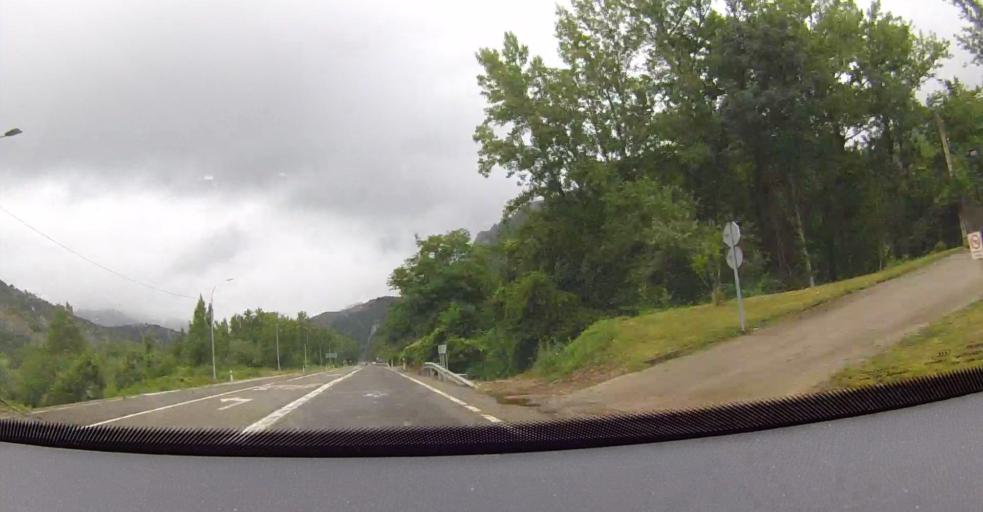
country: ES
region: Castille and Leon
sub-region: Provincia de Leon
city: Cistierna
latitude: 42.8160
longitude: -5.1291
